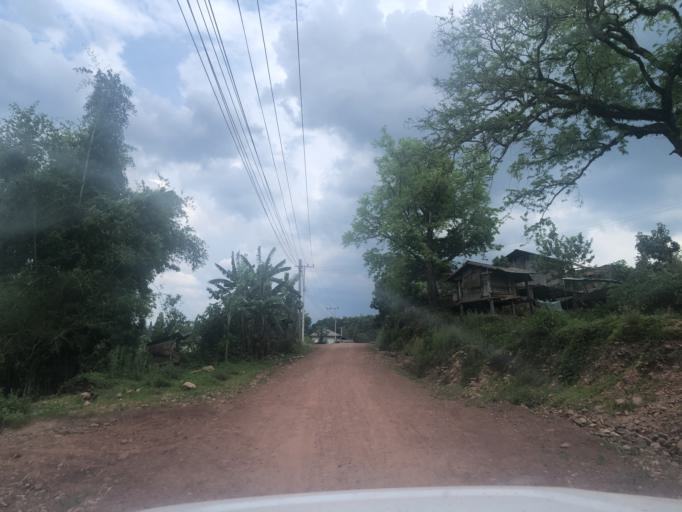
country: LA
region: Phongsali
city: Phongsali
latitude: 21.3093
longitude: 101.9672
